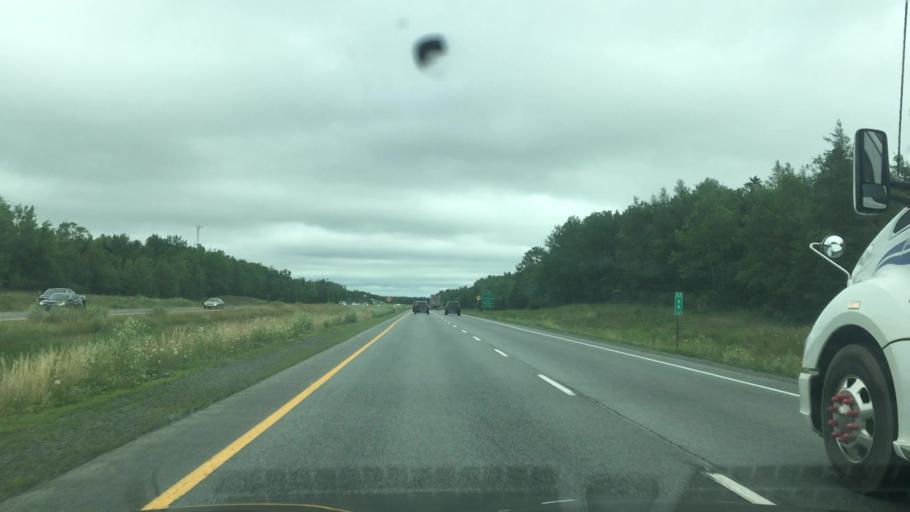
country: CA
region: Nova Scotia
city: Cole Harbour
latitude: 44.9620
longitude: -63.5292
